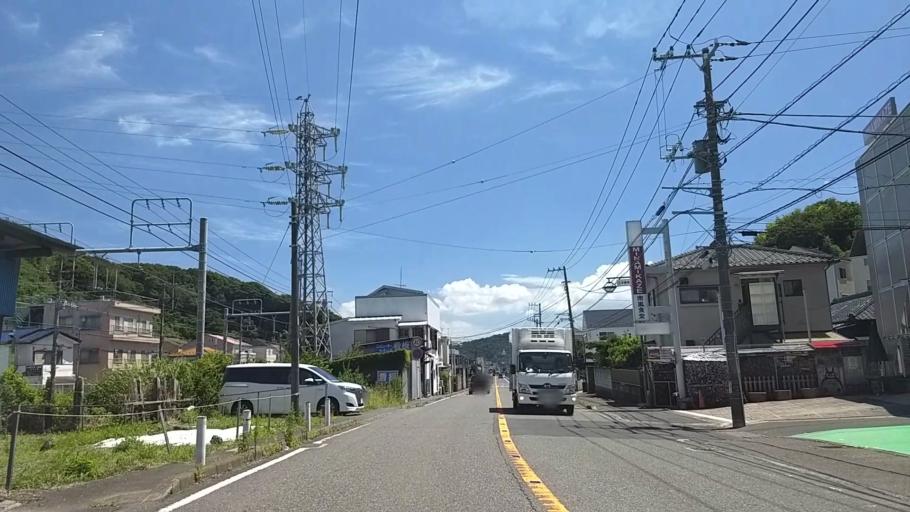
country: JP
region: Kanagawa
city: Zushi
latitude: 35.3048
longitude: 139.5692
